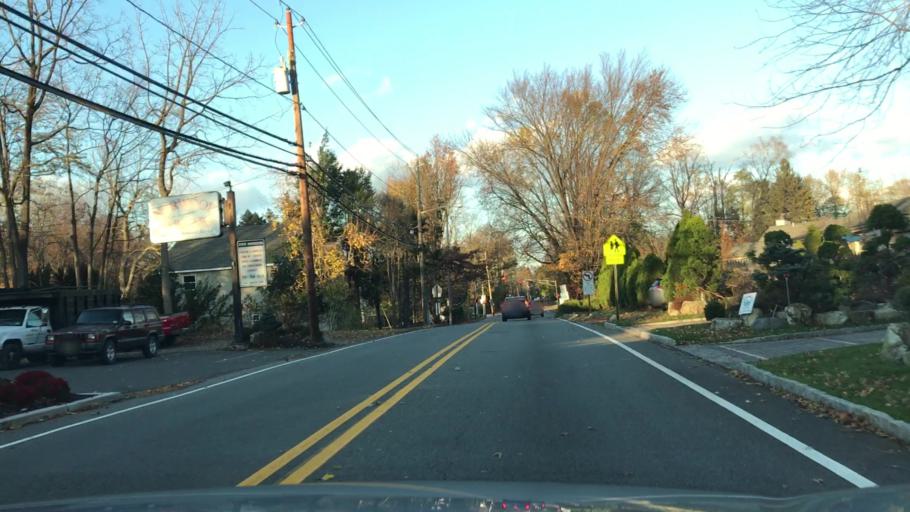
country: US
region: New Jersey
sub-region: Bergen County
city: Norwood
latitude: 40.9932
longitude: -73.9658
